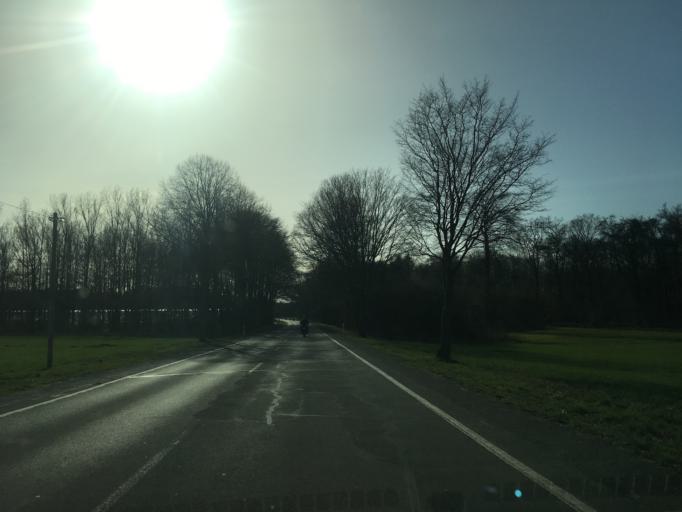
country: DE
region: North Rhine-Westphalia
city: Selm
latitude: 51.7211
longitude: 7.4888
